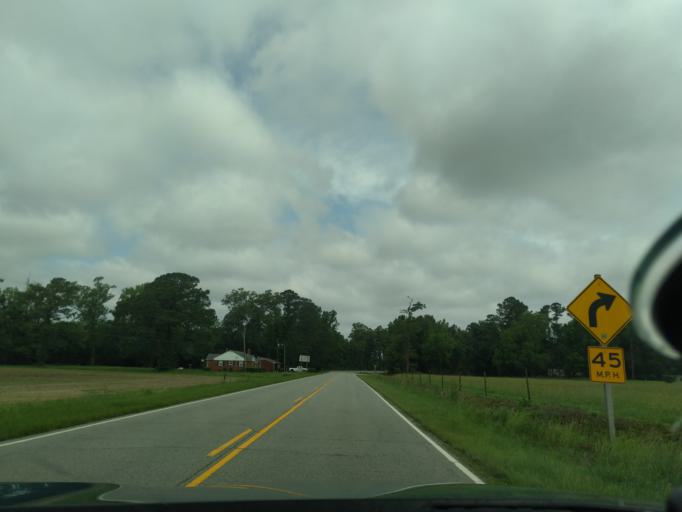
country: US
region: North Carolina
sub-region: Washington County
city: Plymouth
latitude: 35.8938
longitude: -76.6083
